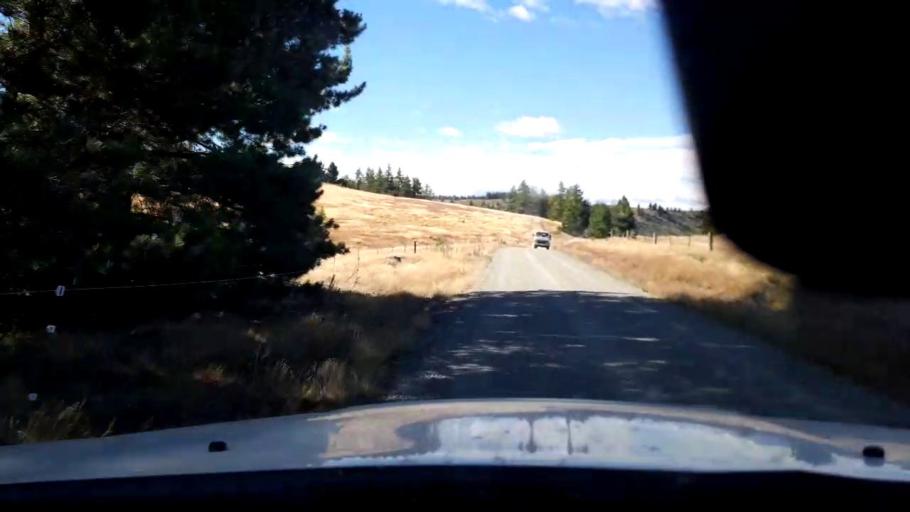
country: NZ
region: Canterbury
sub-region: Timaru District
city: Pleasant Point
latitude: -44.0111
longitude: 170.4724
